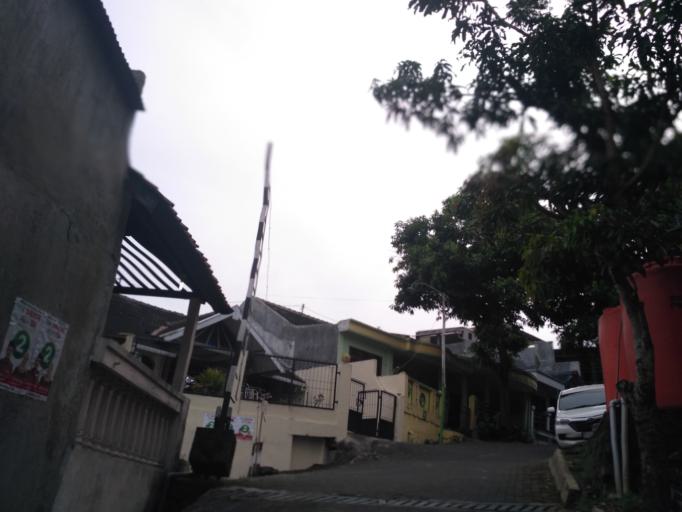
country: ID
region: Central Java
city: Ungaran
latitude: -7.0757
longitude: 110.4282
